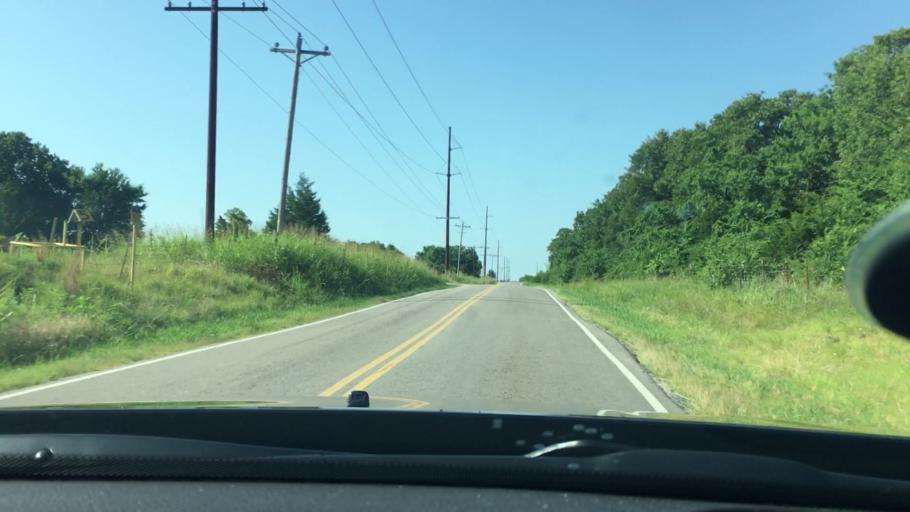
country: US
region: Oklahoma
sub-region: Pontotoc County
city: Ada
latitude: 34.8041
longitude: -96.6348
